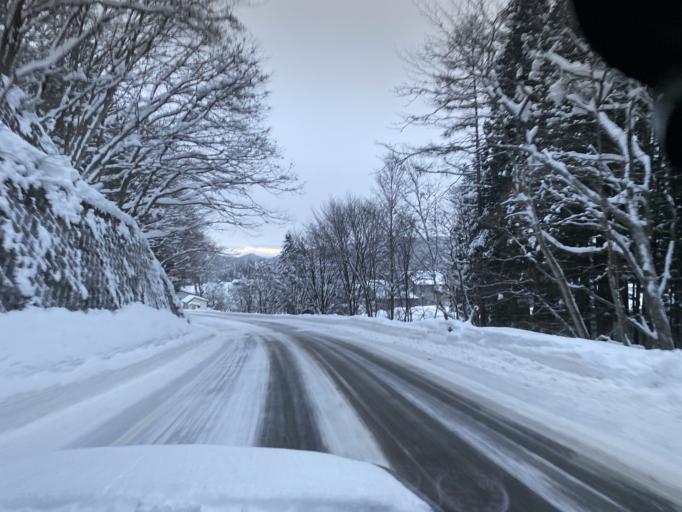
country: JP
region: Nagano
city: Omachi
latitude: 36.5714
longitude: 137.8738
